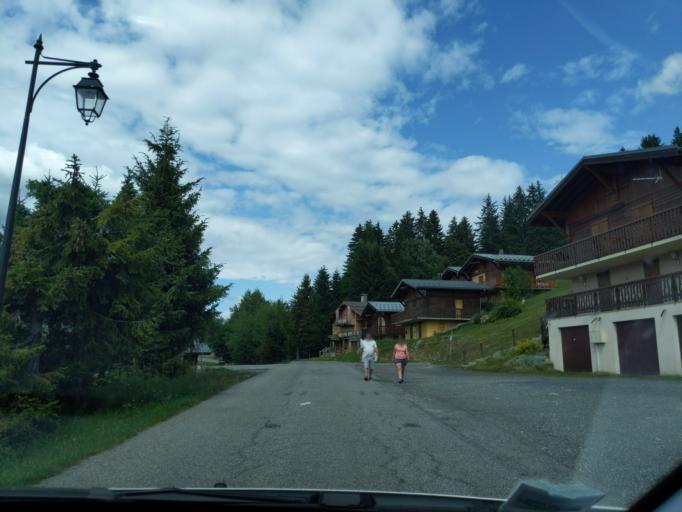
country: FR
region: Rhone-Alpes
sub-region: Departement de la Haute-Savoie
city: Praz-sur-Arly
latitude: 45.7873
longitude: 6.5035
